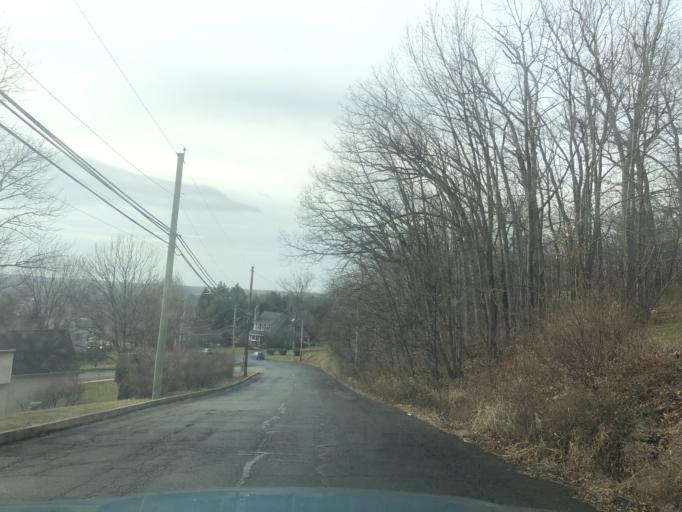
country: US
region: Pennsylvania
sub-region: Bucks County
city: Perkasie
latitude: 40.3814
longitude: -75.2919
